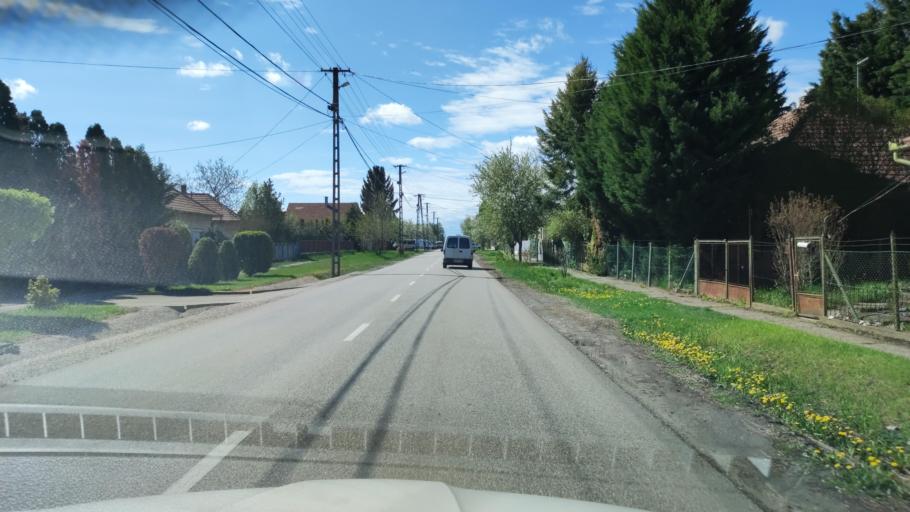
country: HU
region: Pest
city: Abony
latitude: 47.1804
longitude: 20.0058
